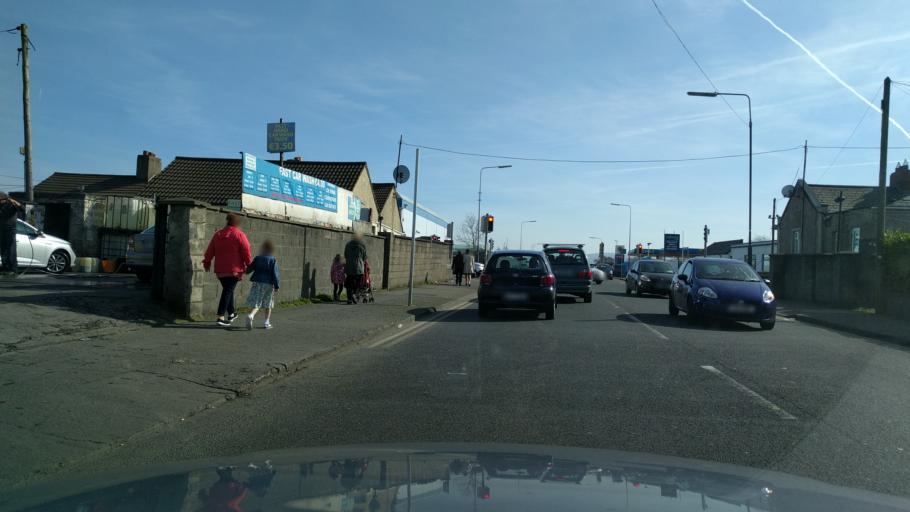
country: IE
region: Leinster
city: Crumlin
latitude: 53.3291
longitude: -6.3443
